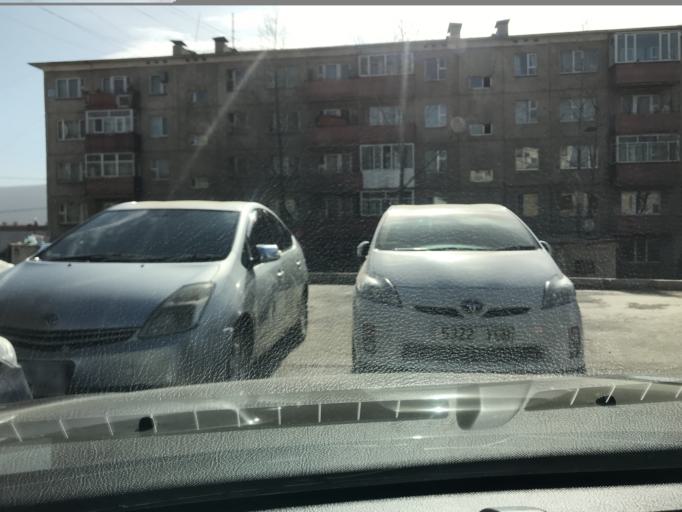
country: MN
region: Ulaanbaatar
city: Ulaanbaatar
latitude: 47.9193
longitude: 106.9518
